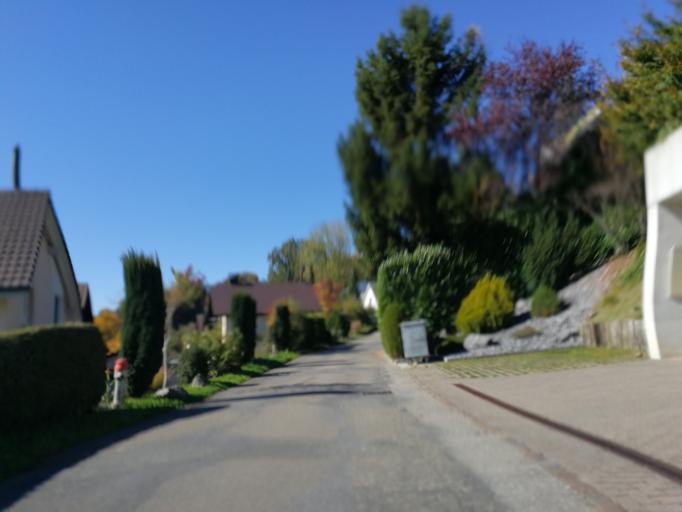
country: CH
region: Zurich
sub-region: Bezirk Meilen
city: Hombrechtikon
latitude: 47.2567
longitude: 8.7811
